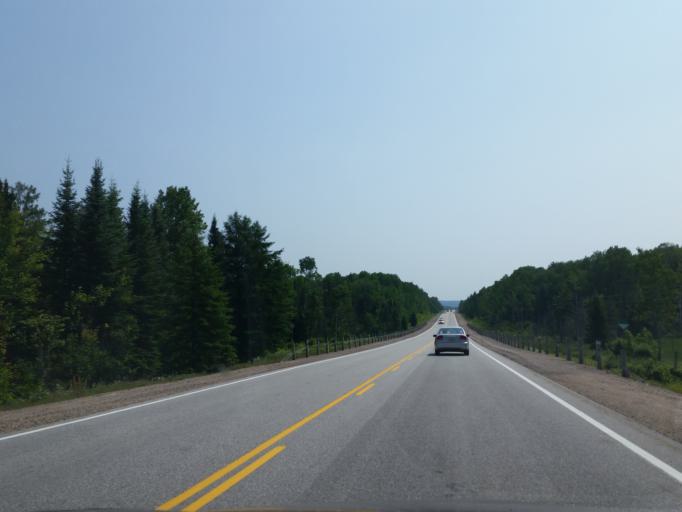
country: CA
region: Ontario
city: Mattawa
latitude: 46.2763
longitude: -78.4597
